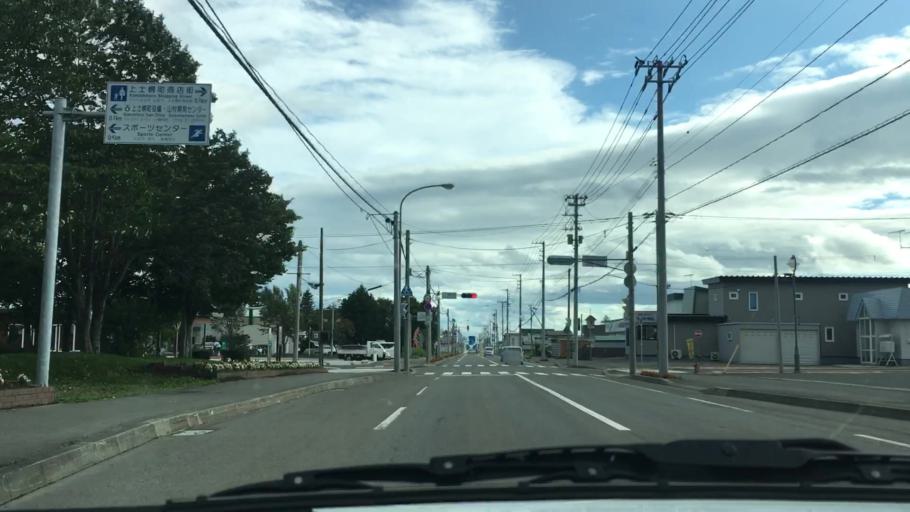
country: JP
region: Hokkaido
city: Otofuke
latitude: 43.2324
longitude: 143.2950
